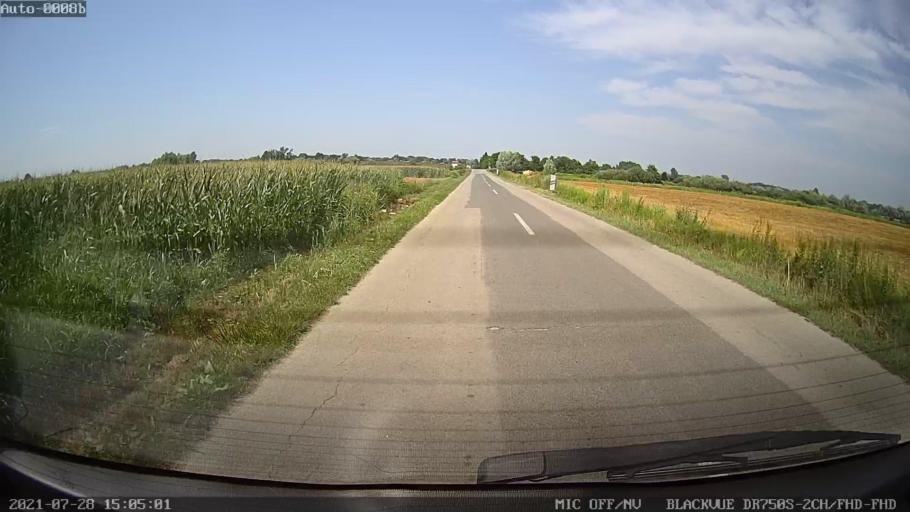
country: HR
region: Varazdinska
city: Jalzabet
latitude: 46.2733
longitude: 16.4339
